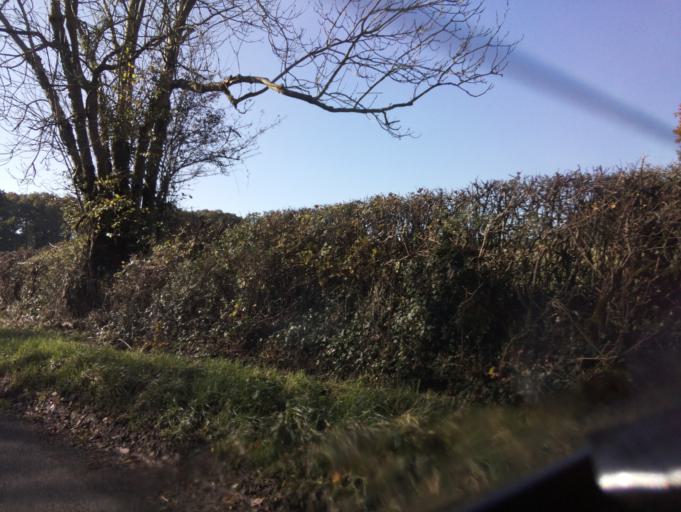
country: GB
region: England
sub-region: Somerset
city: Yeovil
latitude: 50.8858
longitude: -2.5874
